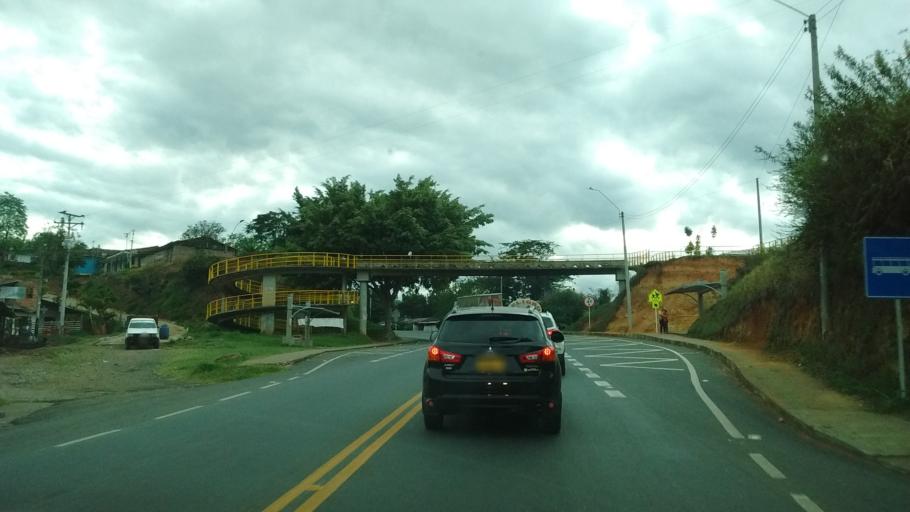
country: CO
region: Cauca
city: Caldono
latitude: 2.7996
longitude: -76.5522
